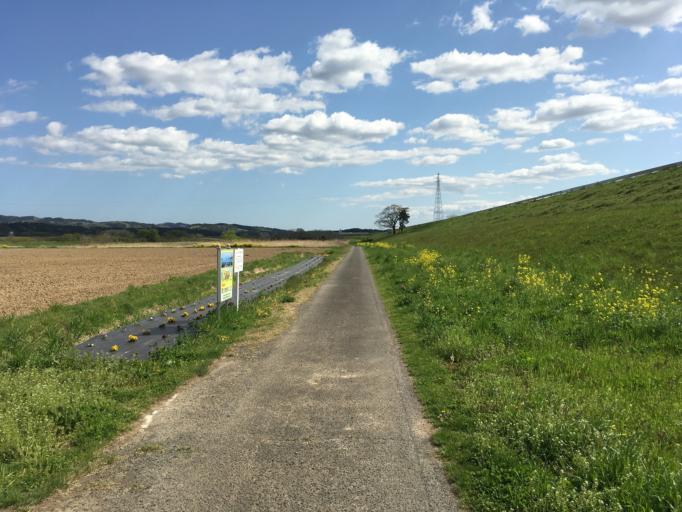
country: JP
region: Miyagi
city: Wakuya
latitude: 38.7198
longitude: 141.2645
